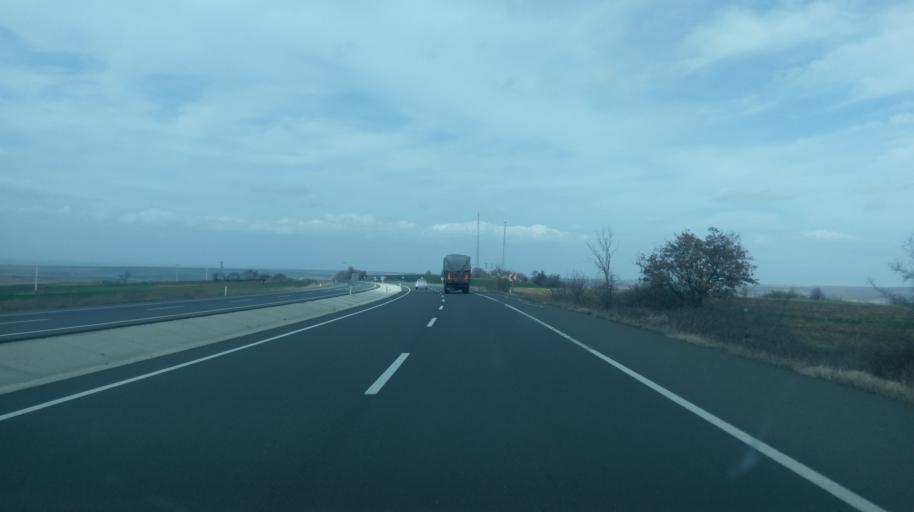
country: TR
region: Edirne
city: Hamidiye
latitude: 41.0915
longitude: 26.6417
